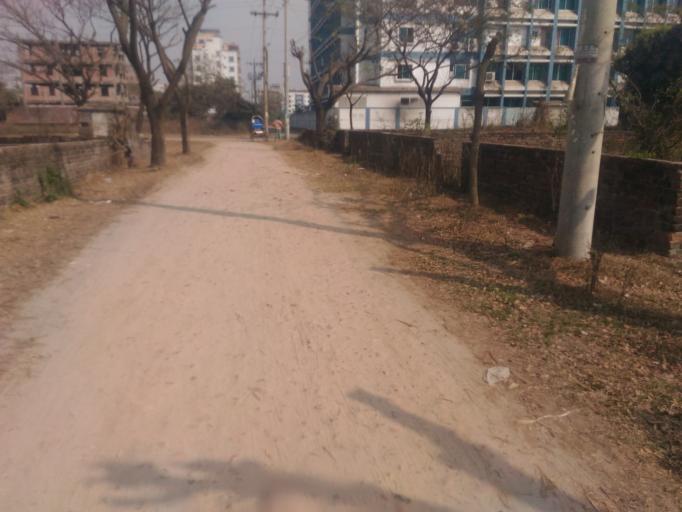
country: BD
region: Dhaka
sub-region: Dhaka
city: Dhaka
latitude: 23.6690
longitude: 90.4250
